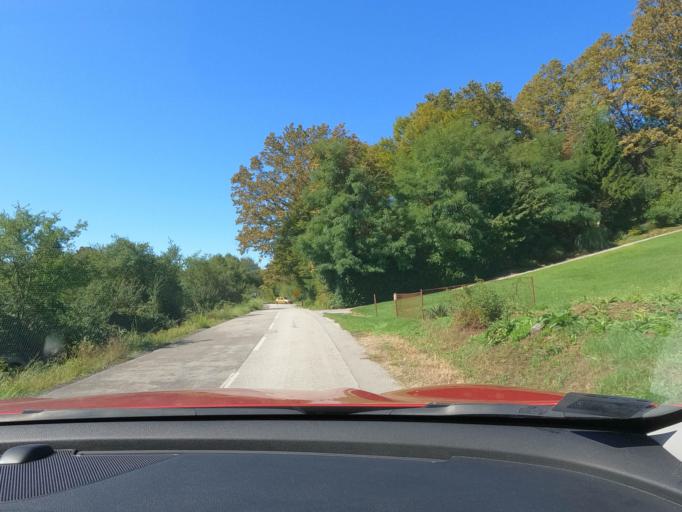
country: HR
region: Sisacko-Moslavacka
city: Petrinja
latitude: 45.4680
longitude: 16.2973
